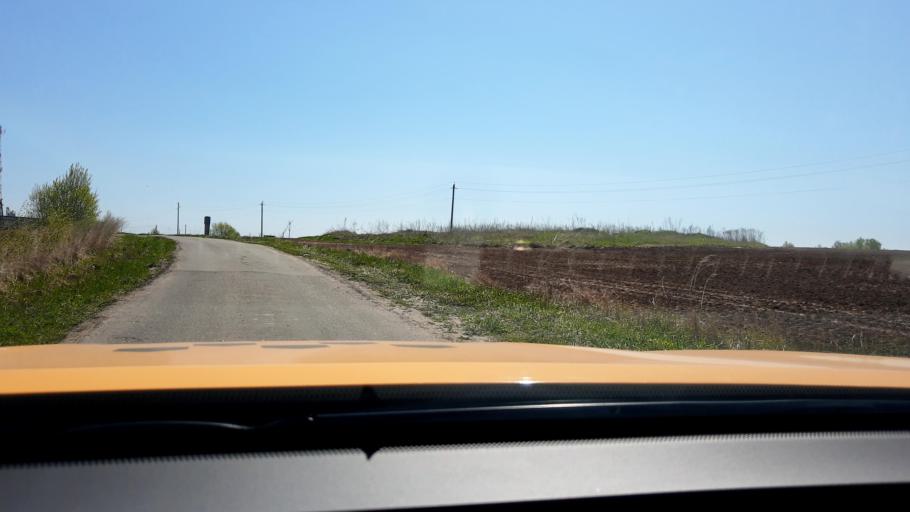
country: RU
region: Moskovskaya
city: Gorki-Leninskiye
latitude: 55.4683
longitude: 37.8313
